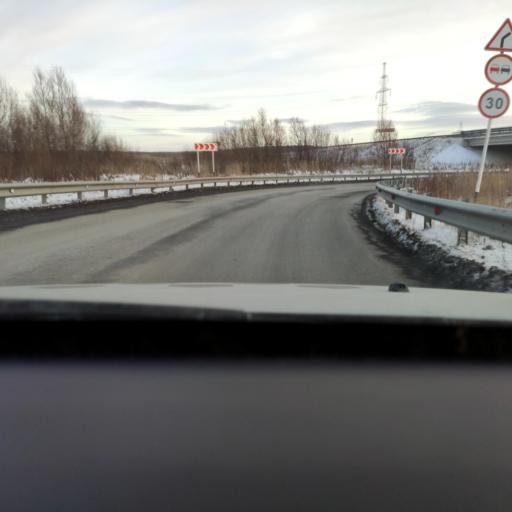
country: RU
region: Perm
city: Ferma
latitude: 57.9317
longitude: 56.3318
